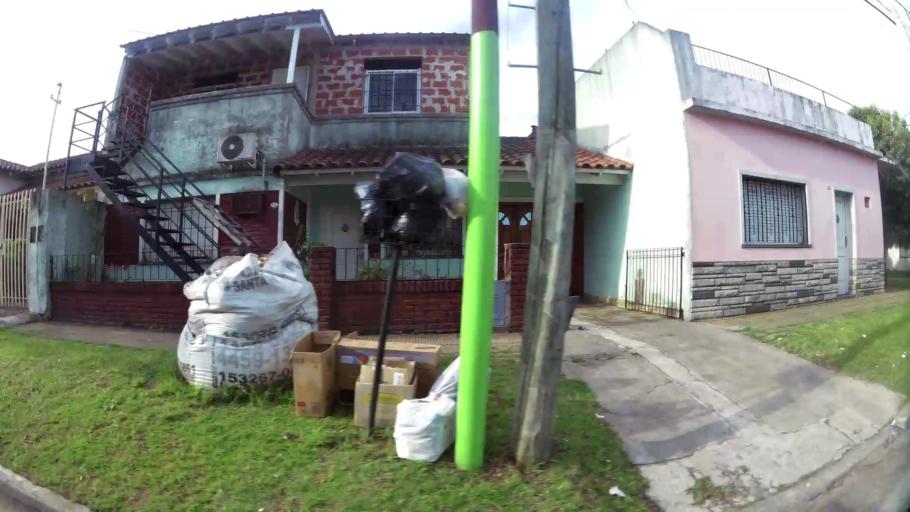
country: AR
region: Buenos Aires
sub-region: Partido de Moron
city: Moron
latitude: -34.6320
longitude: -58.6260
